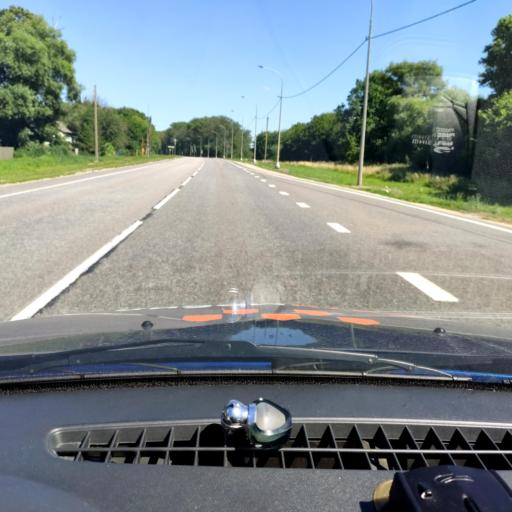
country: RU
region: Orjol
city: Pokrovskoye
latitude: 52.6197
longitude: 36.7408
